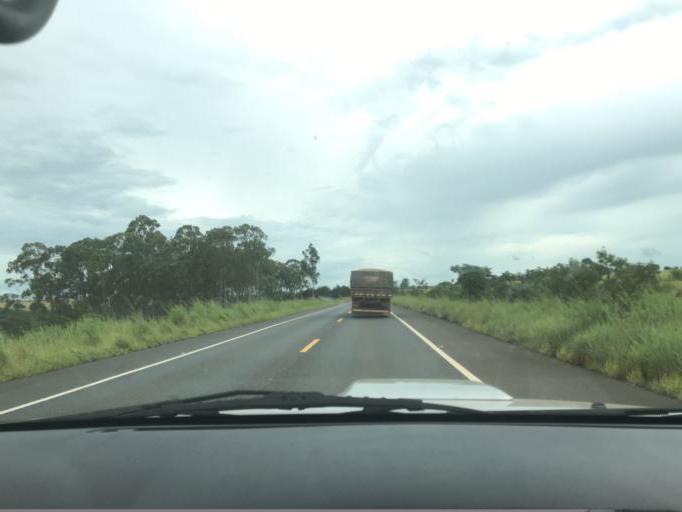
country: BR
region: Minas Gerais
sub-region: Araxa
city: Araxa
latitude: -19.3749
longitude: -46.8573
